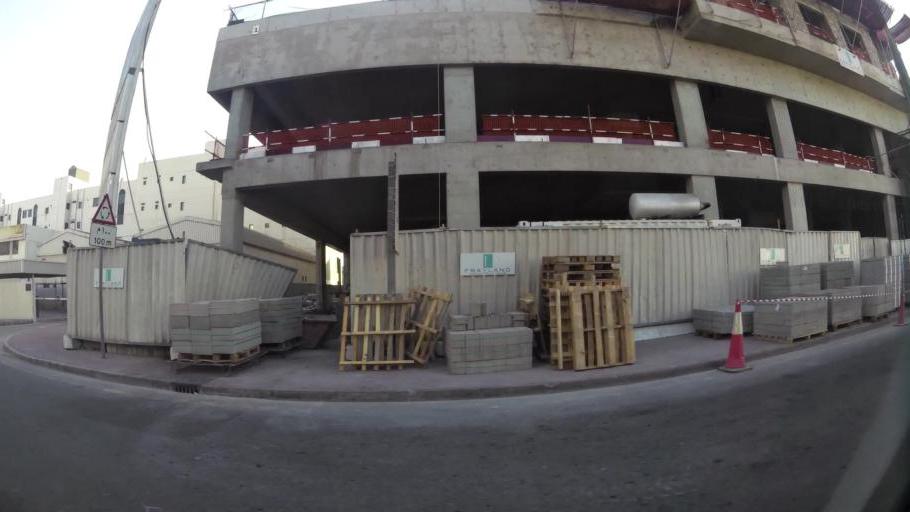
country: AE
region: Ash Shariqah
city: Sharjah
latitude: 25.2508
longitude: 55.3378
